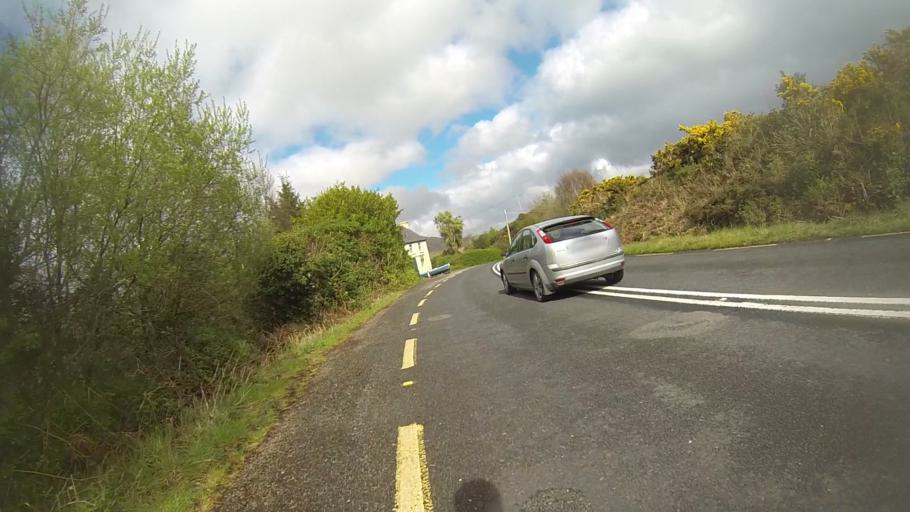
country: IE
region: Munster
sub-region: Ciarrai
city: Kenmare
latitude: 51.8292
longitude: -9.8344
